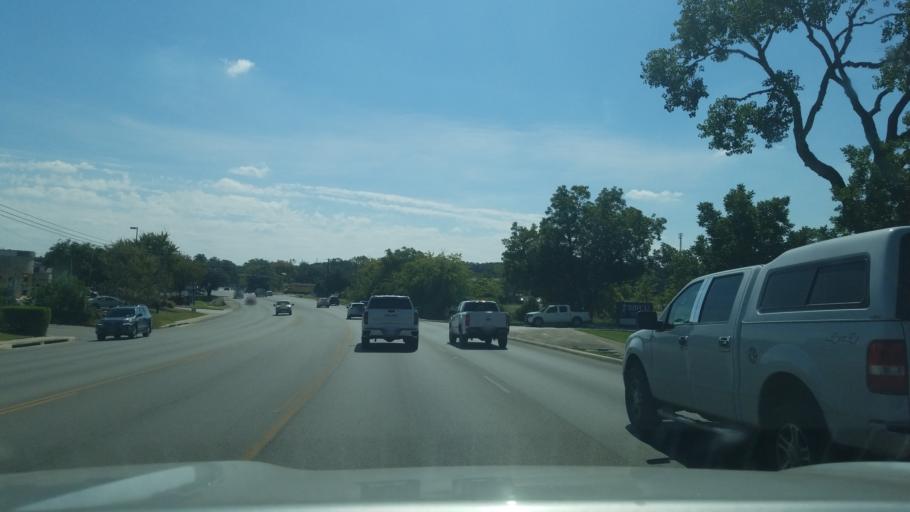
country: US
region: Texas
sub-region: Kendall County
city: Boerne
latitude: 29.7786
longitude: -98.7281
